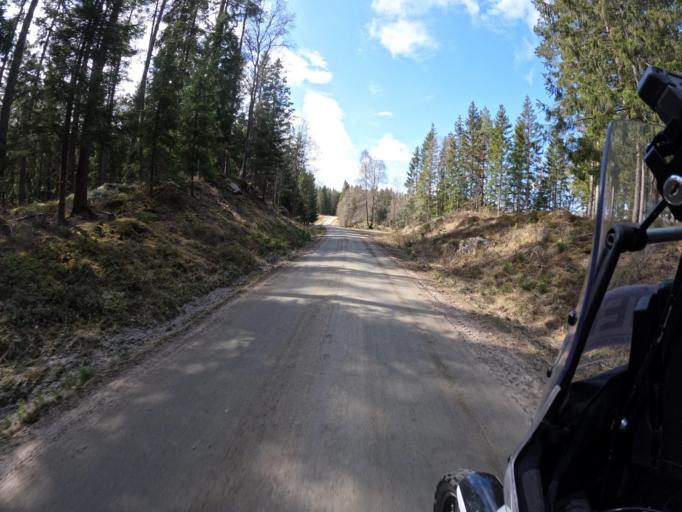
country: SE
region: Vaestra Goetaland
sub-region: Ulricehamns Kommun
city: Ulricehamn
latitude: 57.9228
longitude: 13.5496
